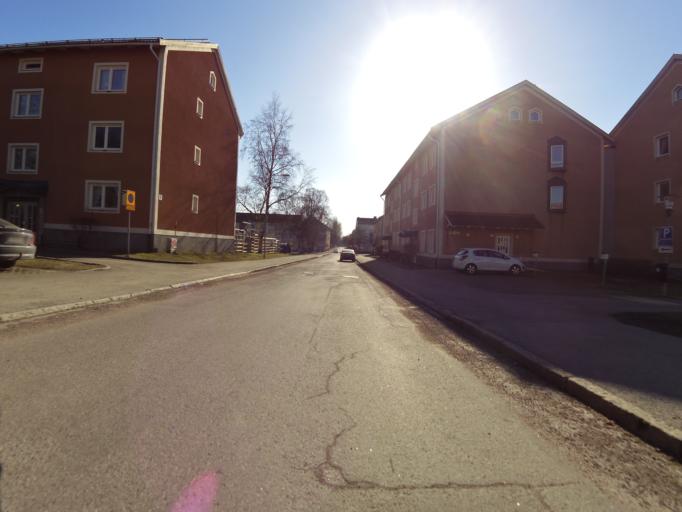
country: SE
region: Gaevleborg
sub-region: Gavle Kommun
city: Gavle
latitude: 60.6720
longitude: 17.1713
